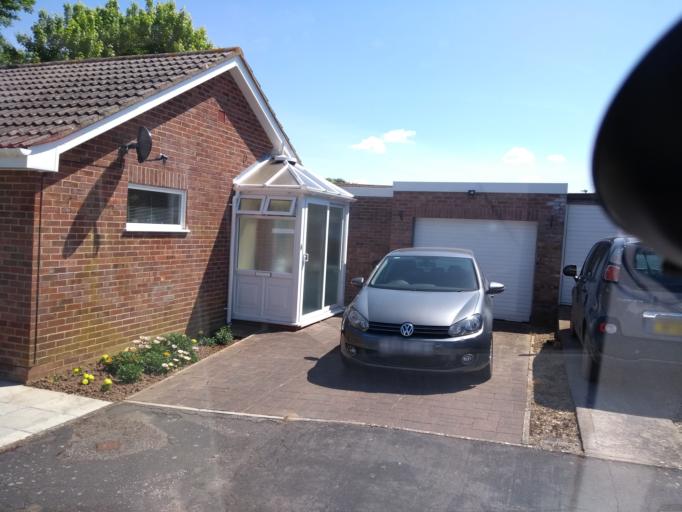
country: GB
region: England
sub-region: Somerset
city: North Petherton
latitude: 51.0900
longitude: -3.0130
